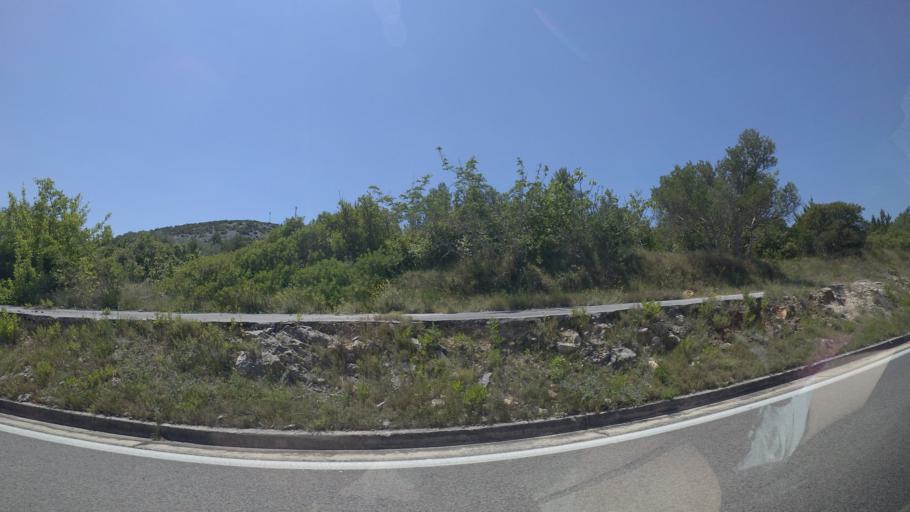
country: HR
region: Sibensko-Kniniska
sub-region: Grad Sibenik
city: Pirovac
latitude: 43.8037
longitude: 15.6724
